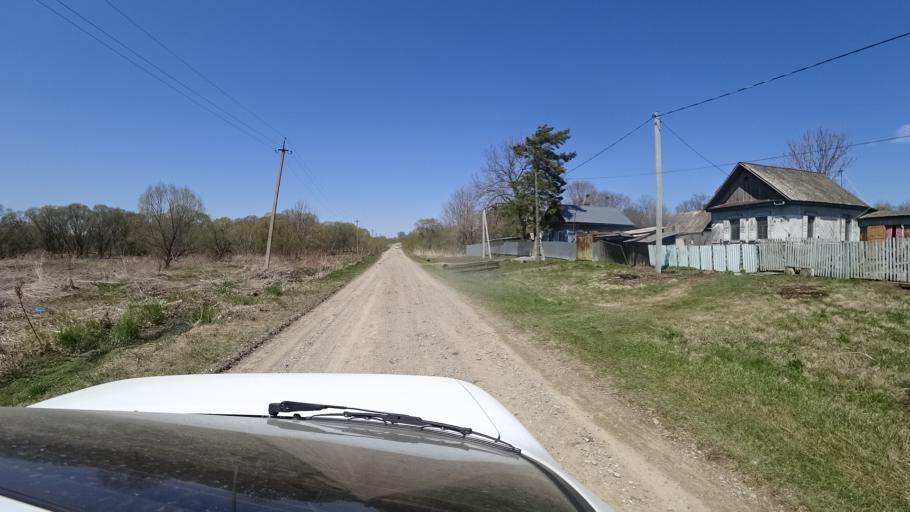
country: RU
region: Primorskiy
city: Lazo
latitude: 45.7938
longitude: 133.7635
